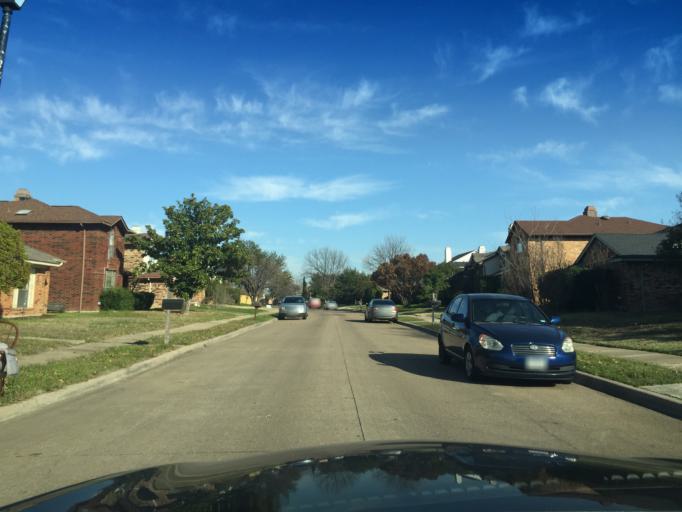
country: US
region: Texas
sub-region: Dallas County
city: Carrollton
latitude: 32.9968
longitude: -96.9003
